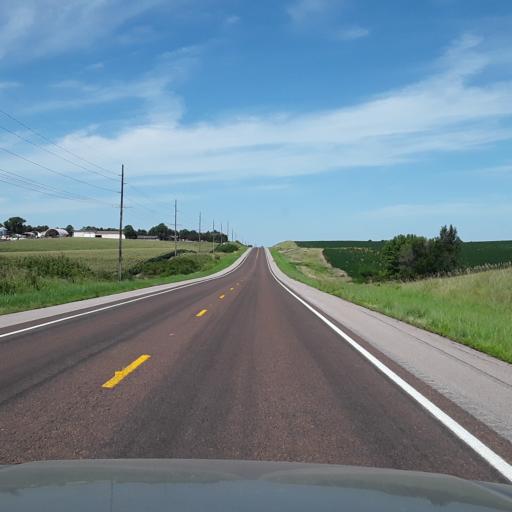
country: US
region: Nebraska
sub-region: Seward County
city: Milford
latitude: 40.8866
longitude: -96.8823
